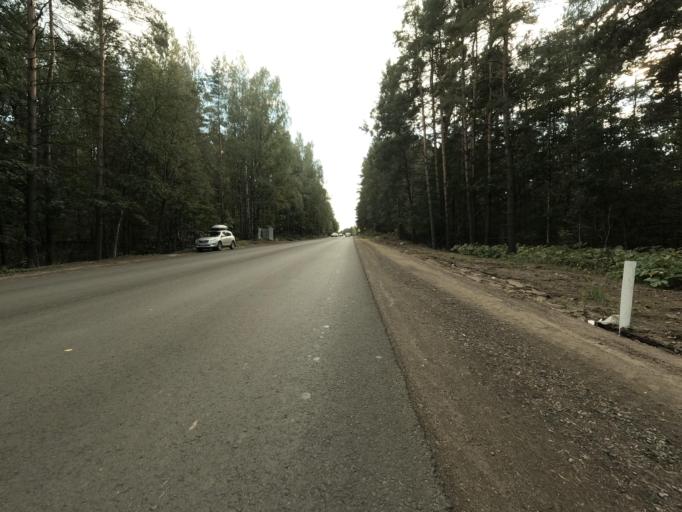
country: RU
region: Leningrad
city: Koltushi
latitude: 59.9571
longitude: 30.6587
